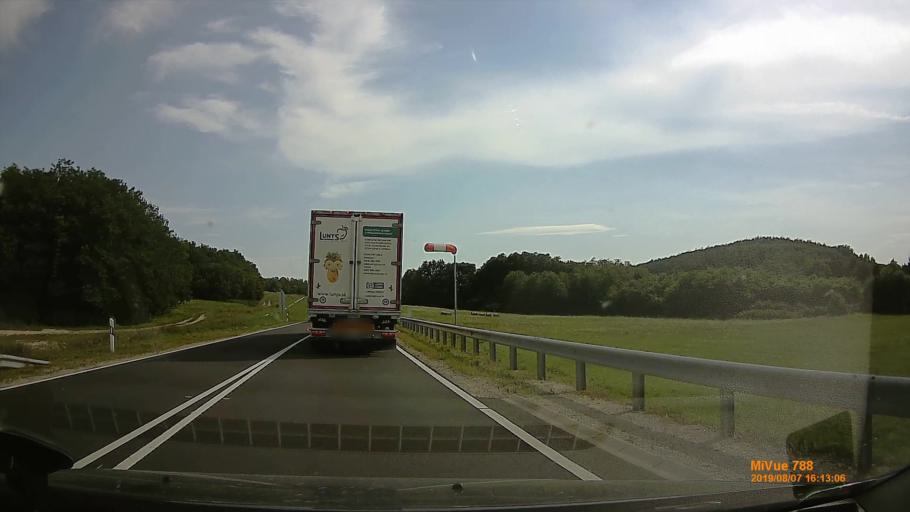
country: HU
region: Zala
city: Zalalovo
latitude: 46.8468
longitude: 16.6297
